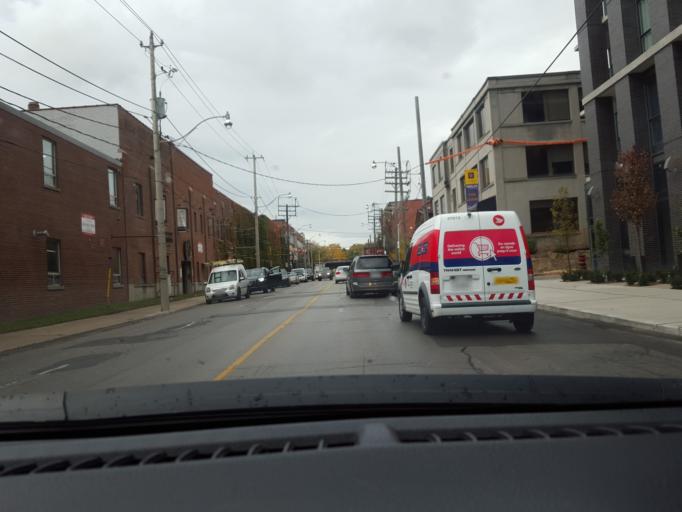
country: CA
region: Ontario
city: Toronto
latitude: 43.6652
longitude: -79.3417
